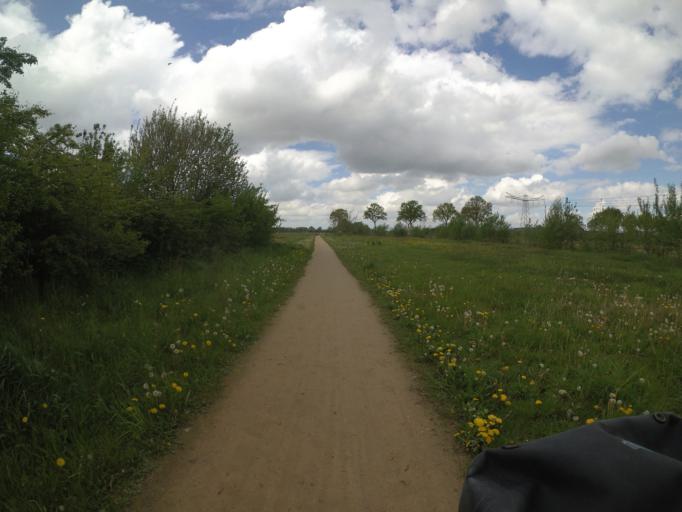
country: NL
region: North Brabant
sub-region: Gemeente Dongen
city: Dongen
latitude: 51.6273
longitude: 4.9709
